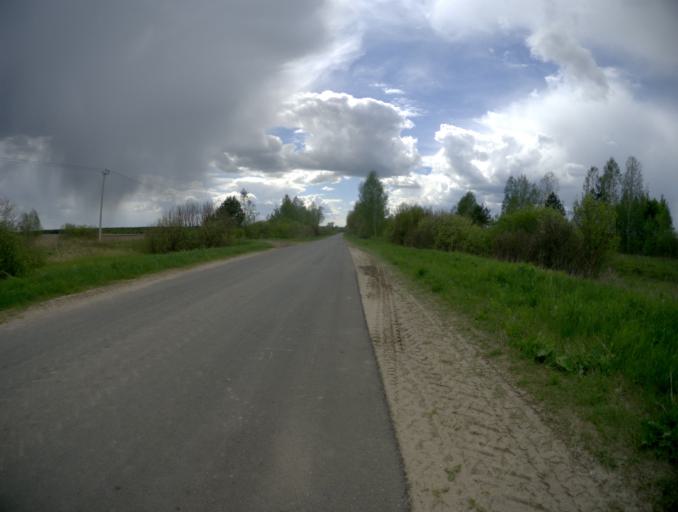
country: RU
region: Vladimir
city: Velikodvorskiy
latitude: 55.2620
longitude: 40.7885
